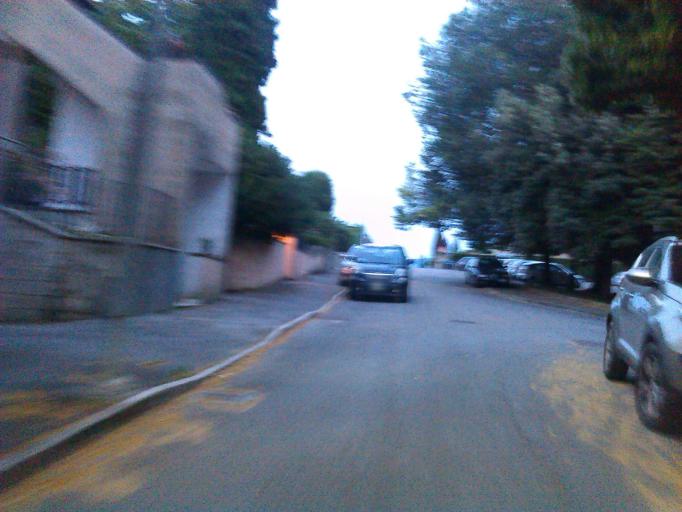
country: IT
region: Tuscany
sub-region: Province of Arezzo
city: Viciomaggio
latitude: 43.4434
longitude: 11.7787
